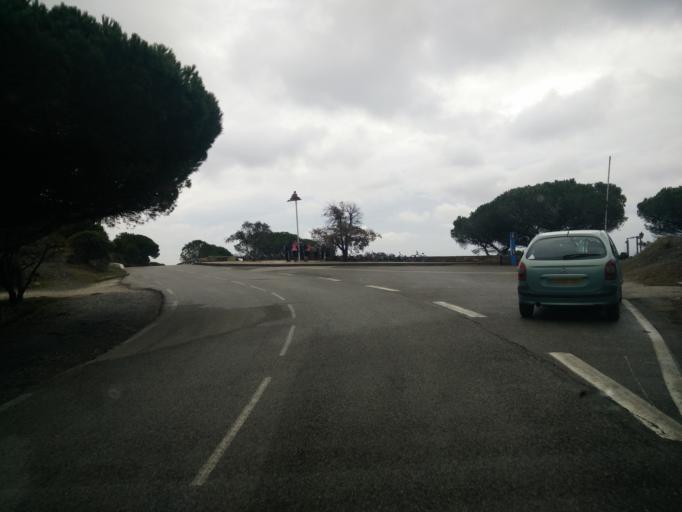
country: FR
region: Provence-Alpes-Cote d'Azur
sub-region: Departement du Var
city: Six-Fours-les-Plages
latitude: 43.0588
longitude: 5.8574
